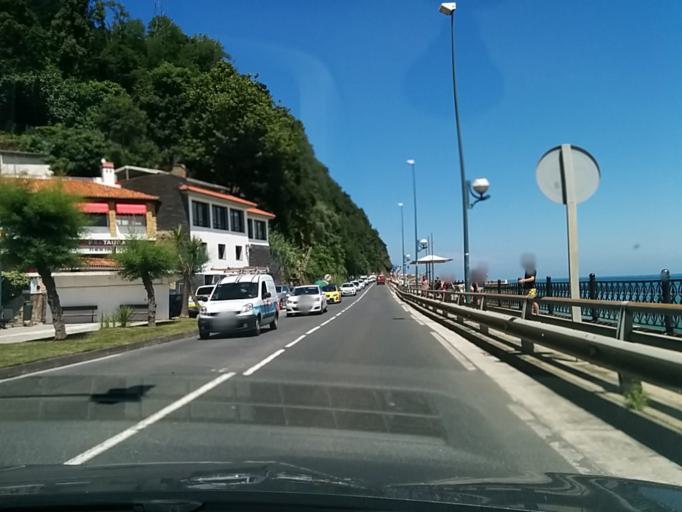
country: ES
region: Basque Country
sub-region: Provincia de Guipuzcoa
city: Zarautz
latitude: 43.2882
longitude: -2.1788
